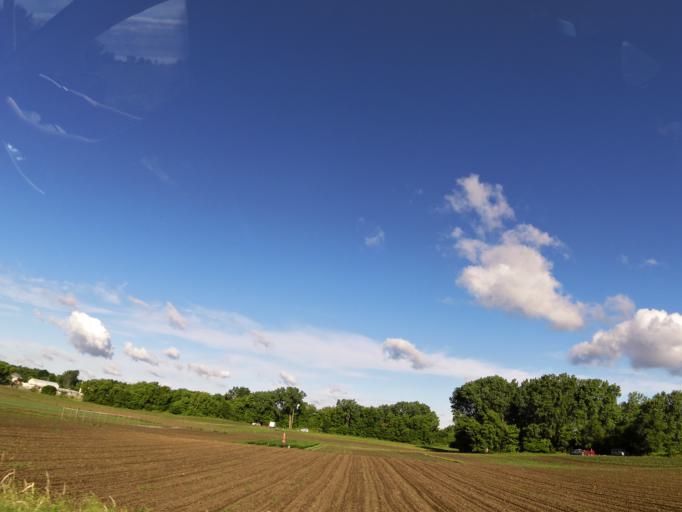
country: US
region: Minnesota
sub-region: Dakota County
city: Hastings
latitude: 44.7823
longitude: -92.8629
